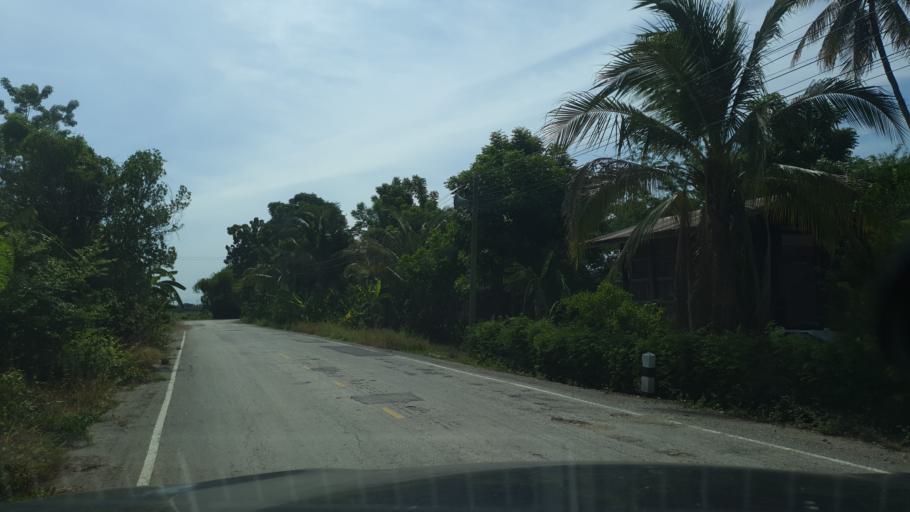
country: TH
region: Sukhothai
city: Si Samrong
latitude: 17.1989
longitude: 99.7215
